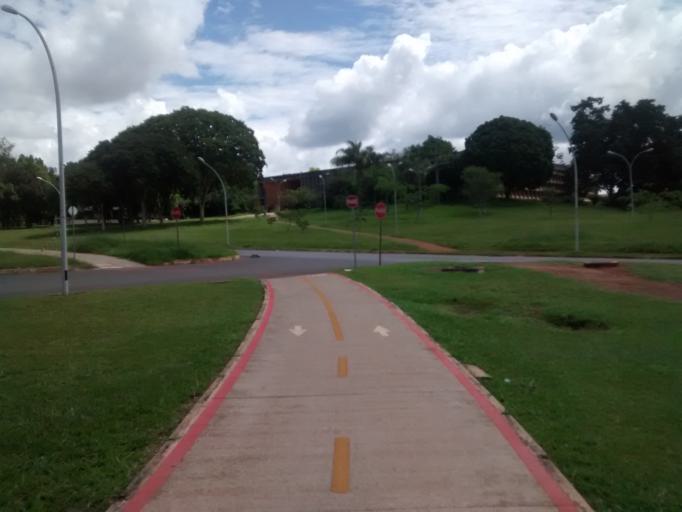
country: BR
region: Federal District
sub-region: Brasilia
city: Brasilia
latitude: -15.7605
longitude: -47.8710
